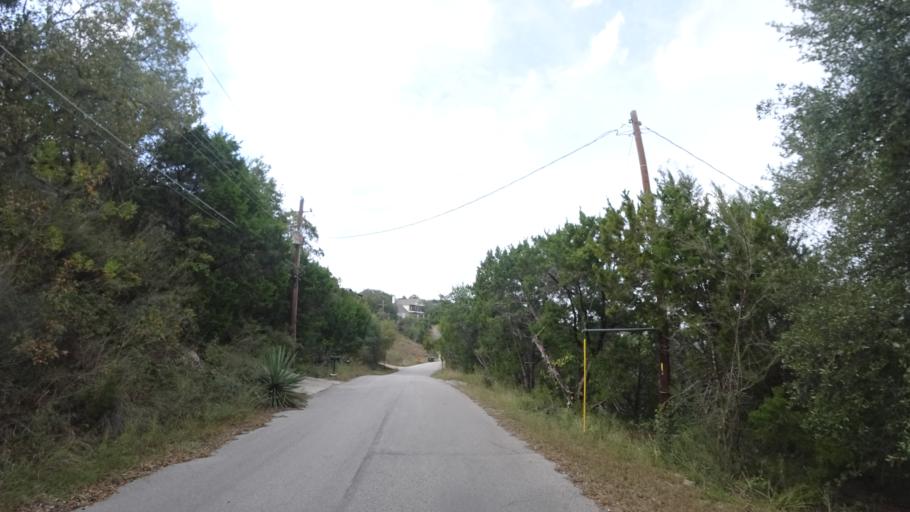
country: US
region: Texas
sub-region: Travis County
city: Hudson Bend
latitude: 30.3743
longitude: -97.9172
